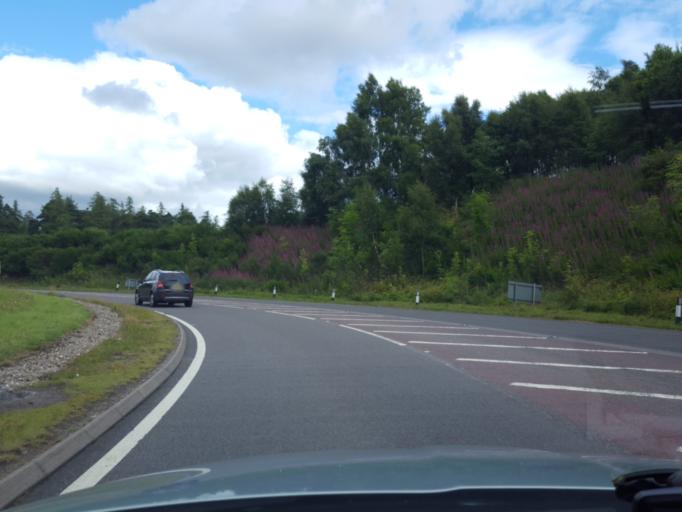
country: GB
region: Scotland
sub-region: Moray
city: Rothes
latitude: 57.4022
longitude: -3.3575
